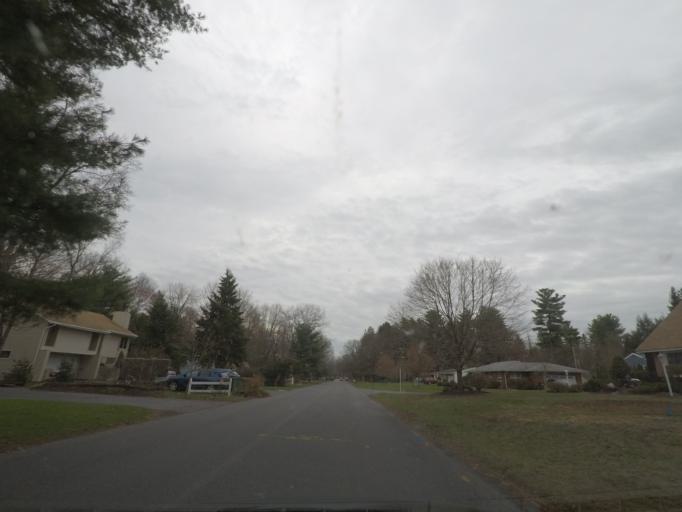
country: US
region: New York
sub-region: Albany County
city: Delmar
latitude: 42.6081
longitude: -73.8369
